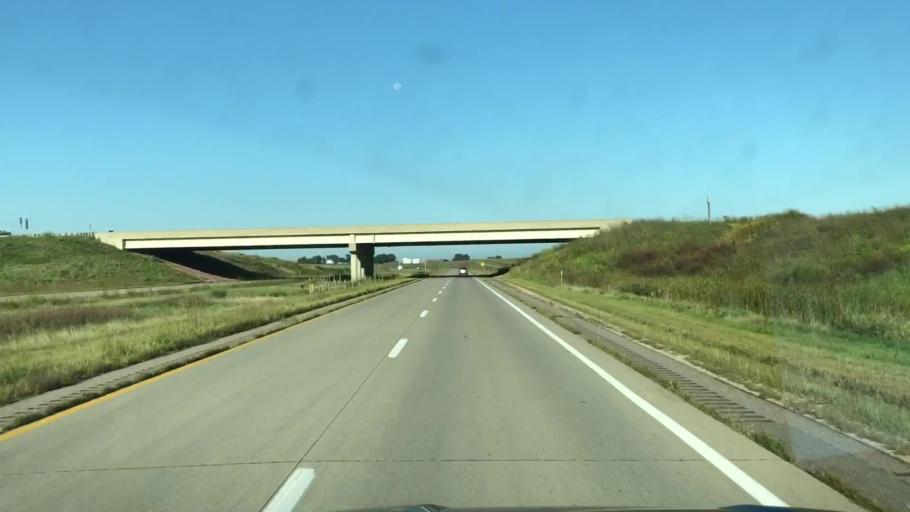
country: US
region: Iowa
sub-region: Plymouth County
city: Le Mars
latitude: 42.8184
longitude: -96.1732
